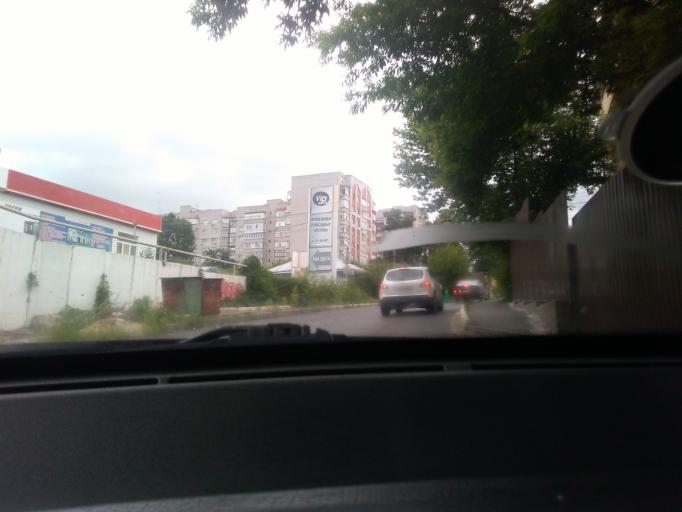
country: RU
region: Kursk
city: Kursk
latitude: 51.7390
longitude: 36.1844
